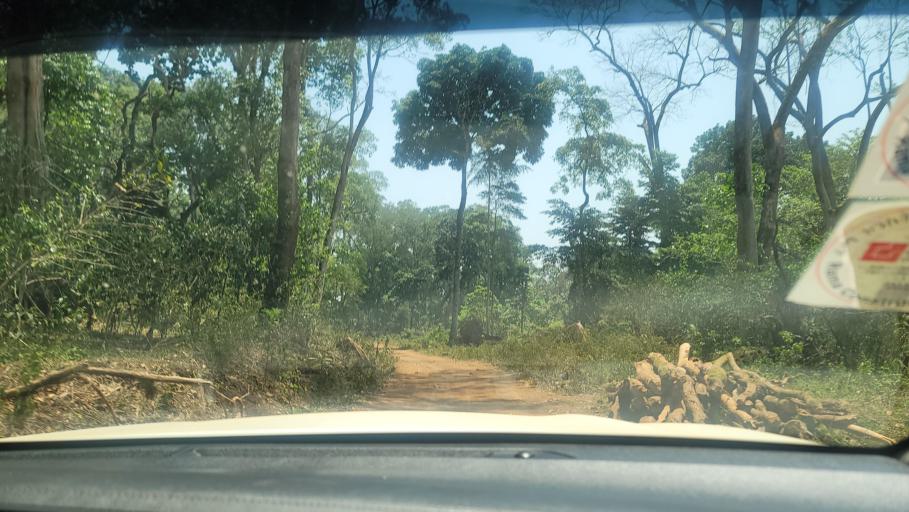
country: ET
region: Southern Nations, Nationalities, and People's Region
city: Bonga
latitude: 7.5083
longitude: 36.2257
